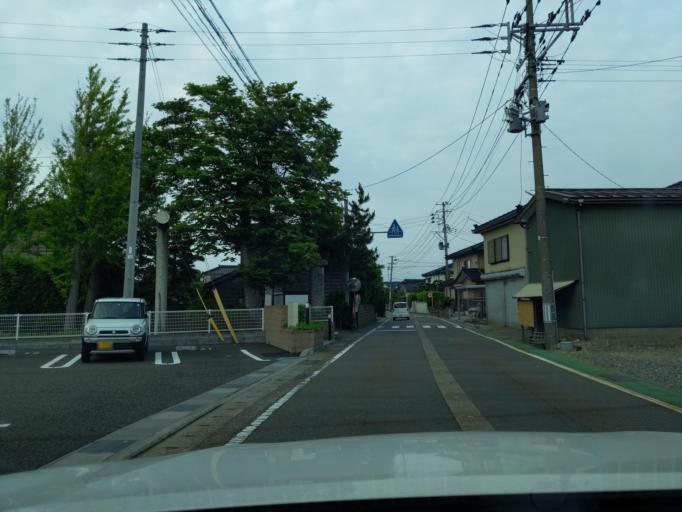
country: JP
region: Niigata
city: Kashiwazaki
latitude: 37.3811
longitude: 138.5719
